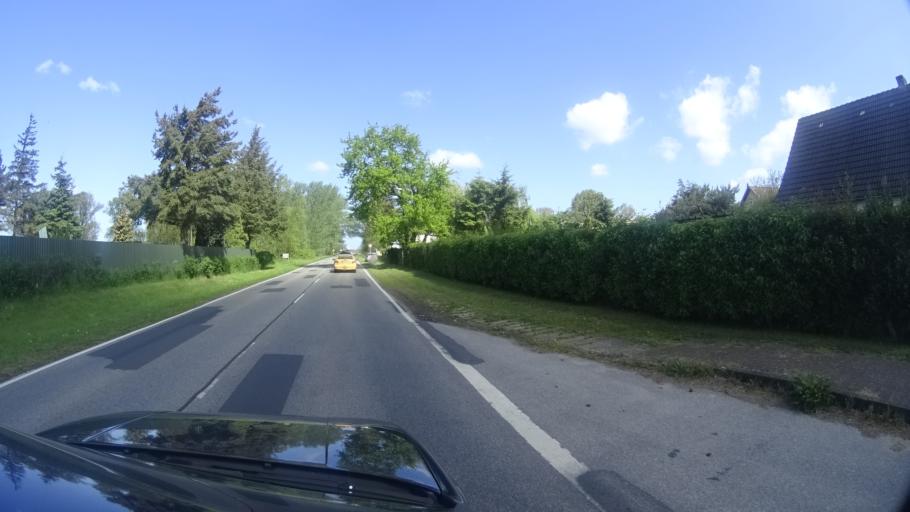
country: DE
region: Mecklenburg-Vorpommern
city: Zingst
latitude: 54.4028
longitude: 12.6767
